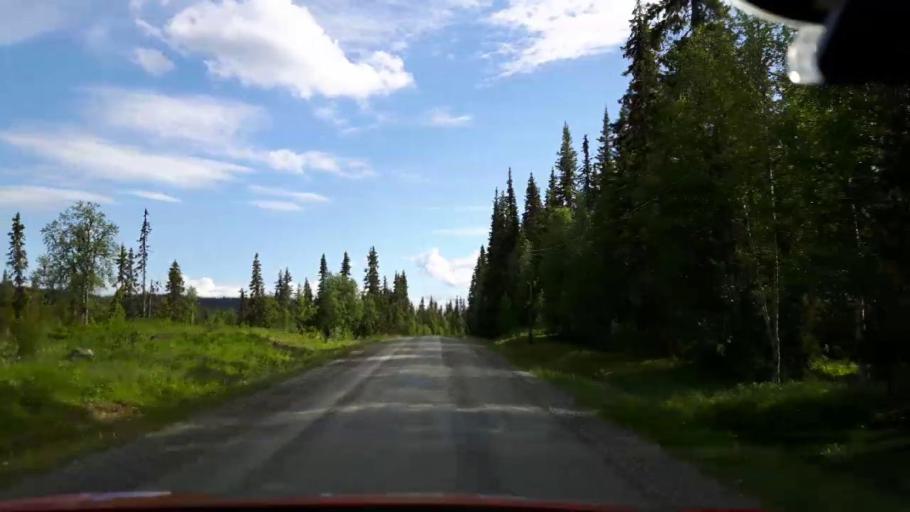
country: SE
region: Jaemtland
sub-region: Krokoms Kommun
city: Valla
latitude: 63.8095
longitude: 14.0496
